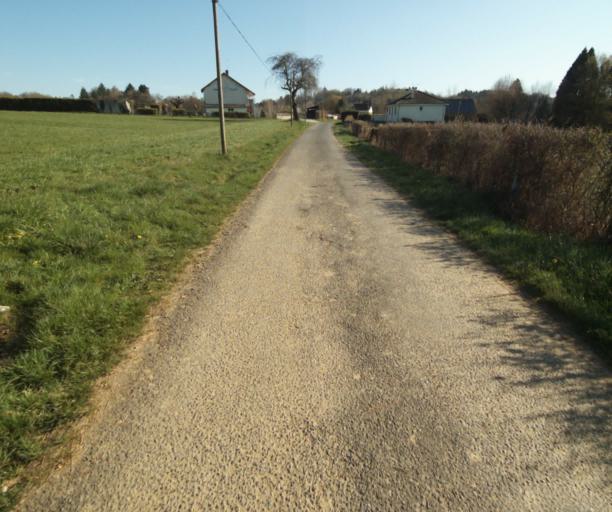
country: FR
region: Limousin
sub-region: Departement de la Correze
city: Chamboulive
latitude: 45.4732
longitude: 1.7245
